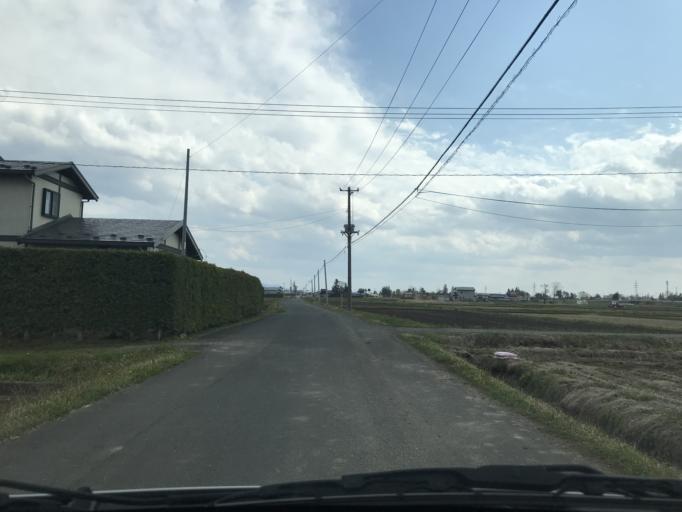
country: JP
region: Iwate
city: Mizusawa
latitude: 39.1799
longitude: 141.1254
